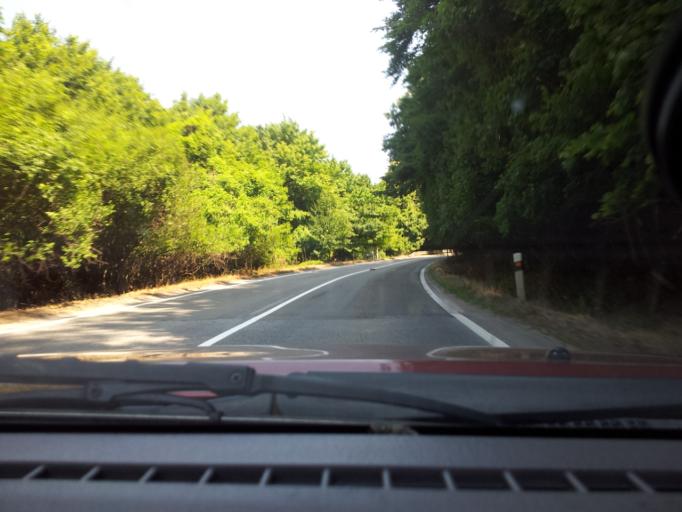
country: SK
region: Trnavsky
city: Smolenice
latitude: 48.5477
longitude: 17.4497
